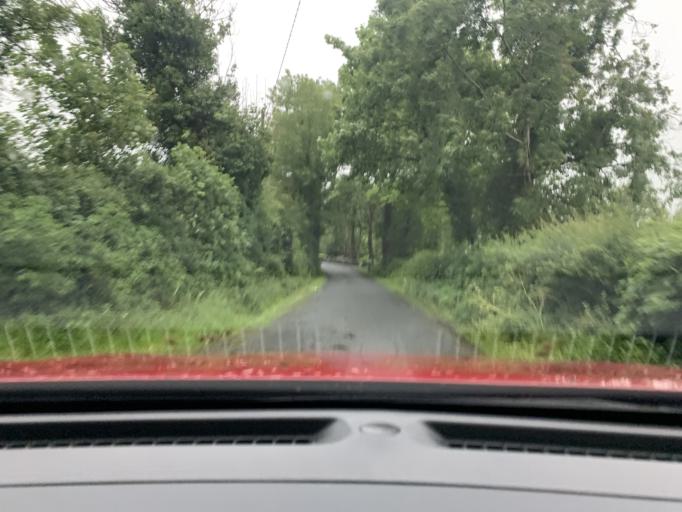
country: IE
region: Connaught
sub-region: Sligo
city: Sligo
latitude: 54.3192
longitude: -8.4673
